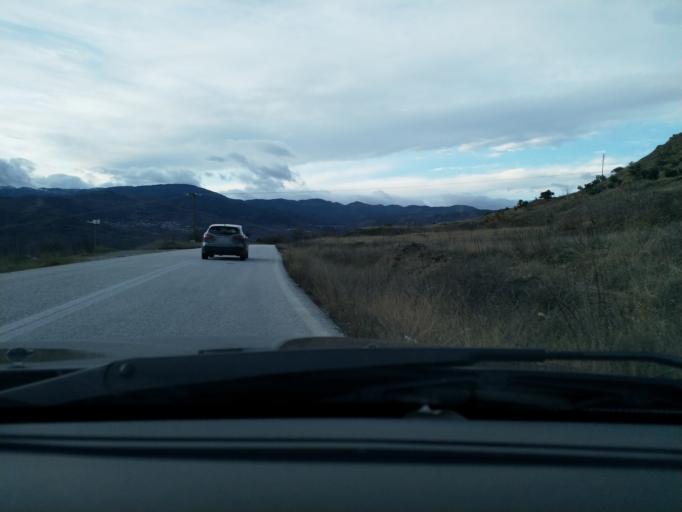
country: GR
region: Epirus
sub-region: Nomos Ioanninon
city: Metsovo
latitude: 39.7862
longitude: 21.3816
